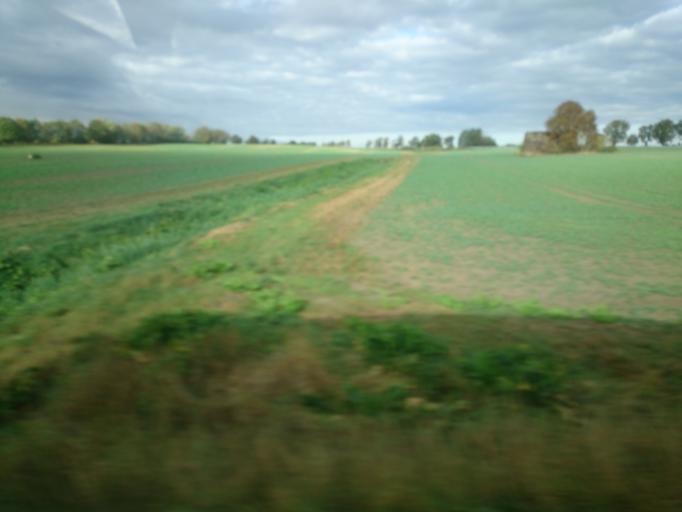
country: DE
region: Mecklenburg-Vorpommern
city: Pasewalk
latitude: 53.5126
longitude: 13.9769
